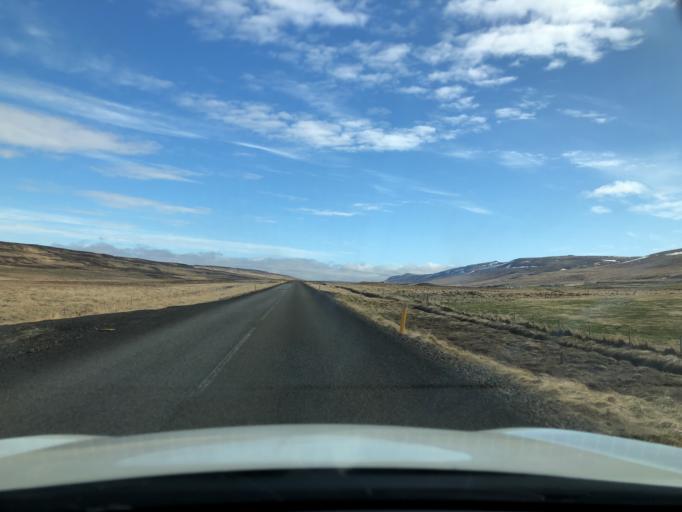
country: IS
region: West
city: Borgarnes
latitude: 65.1209
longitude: -21.6671
